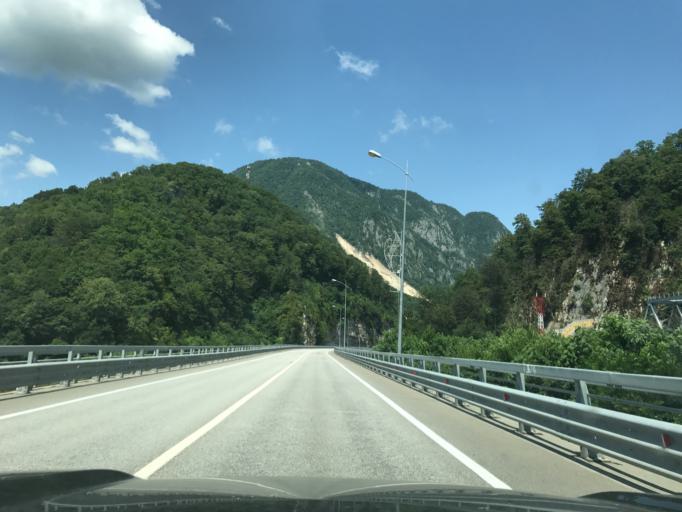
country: RU
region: Krasnodarskiy
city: Vysokoye
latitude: 43.5801
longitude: 40.0090
